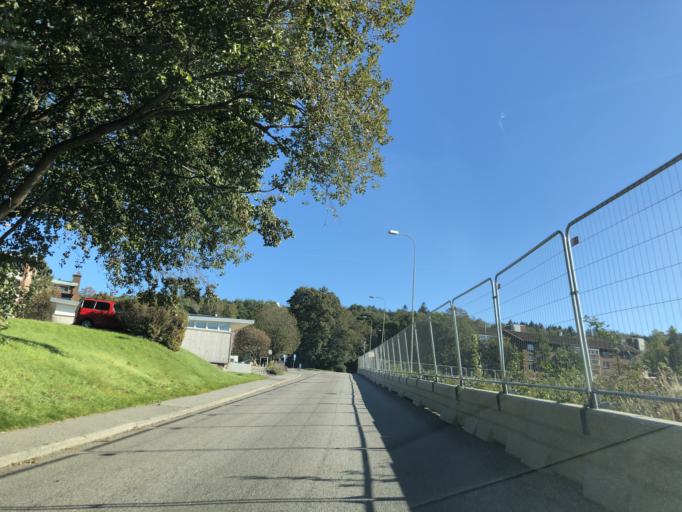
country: SE
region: Vaestra Goetaland
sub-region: Molndal
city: Moelndal
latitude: 57.6807
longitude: 12.0132
